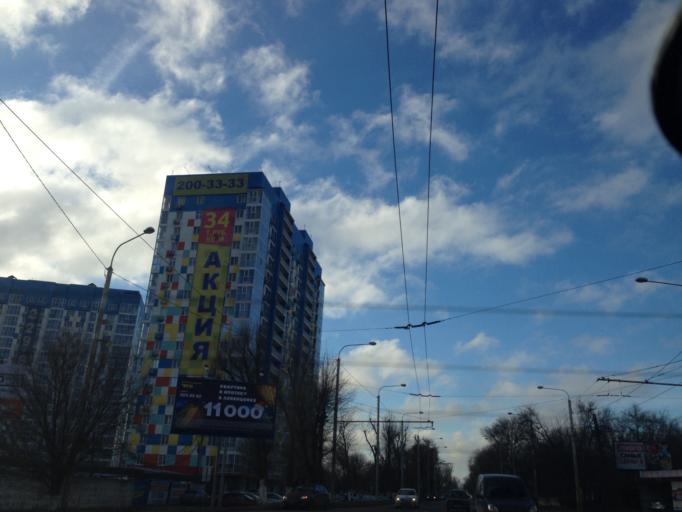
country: RU
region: Rostov
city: Severnyy
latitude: 47.2571
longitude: 39.6400
